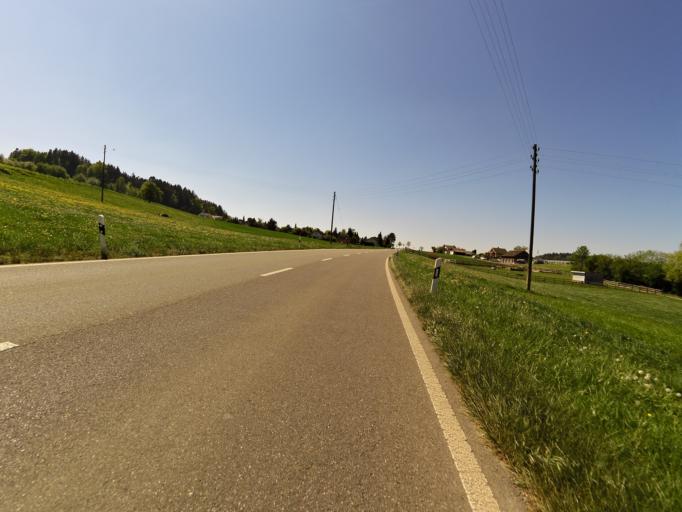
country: CH
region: Thurgau
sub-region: Frauenfeld District
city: Gachnang
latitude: 47.5419
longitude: 8.8331
